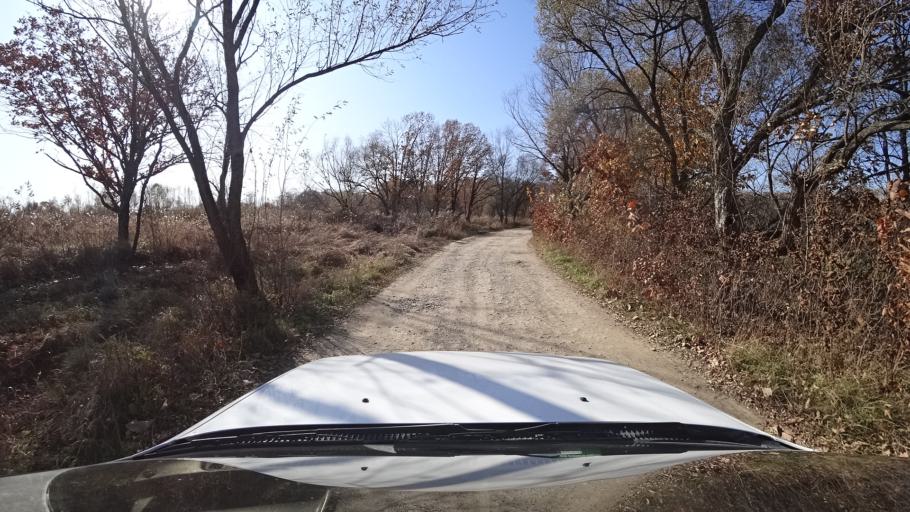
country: RU
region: Primorskiy
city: Dal'nerechensk
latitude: 45.8832
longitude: 133.7383
